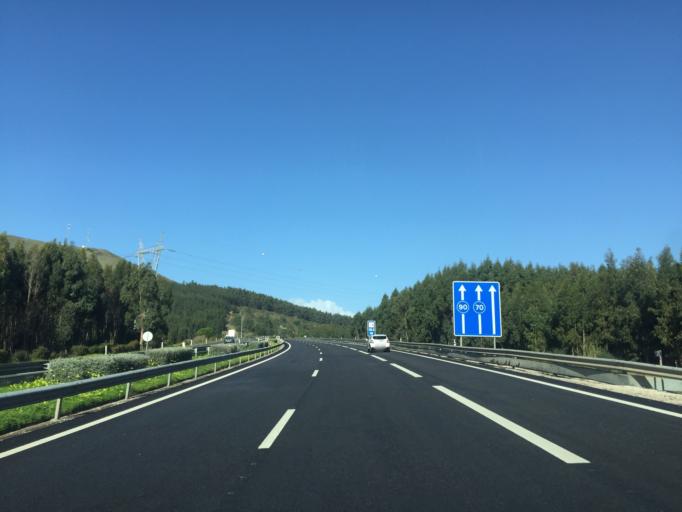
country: PT
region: Lisbon
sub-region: Sobral de Monte Agraco
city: Sobral de Monte Agraco
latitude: 39.0142
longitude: -9.2132
